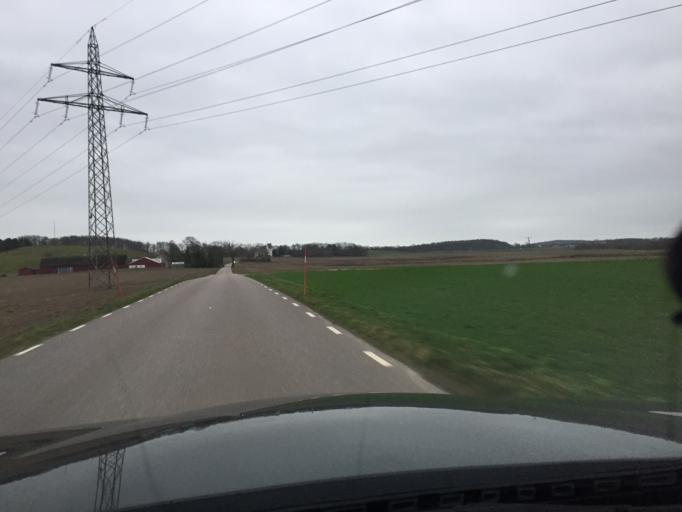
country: SE
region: Skane
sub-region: Malmo
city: Oxie
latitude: 55.5558
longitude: 13.1634
